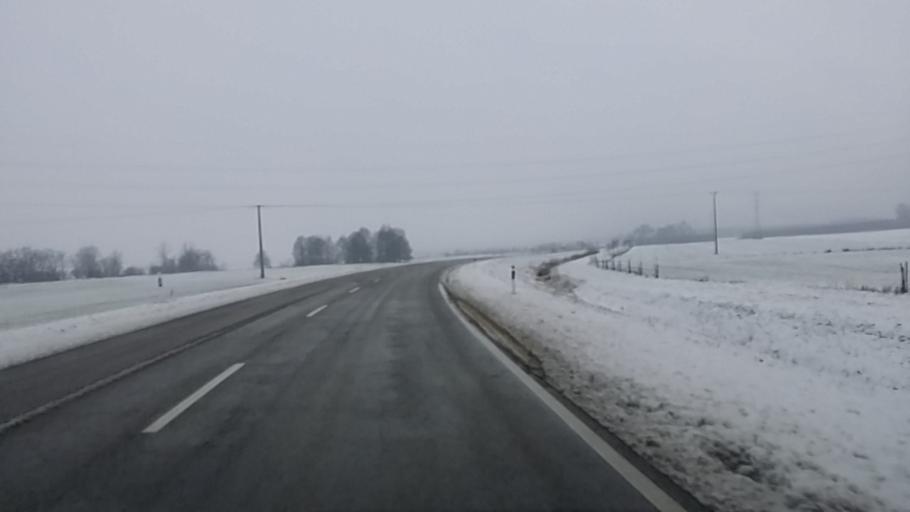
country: HU
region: Komarom-Esztergom
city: Komarom
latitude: 47.7202
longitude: 18.1117
